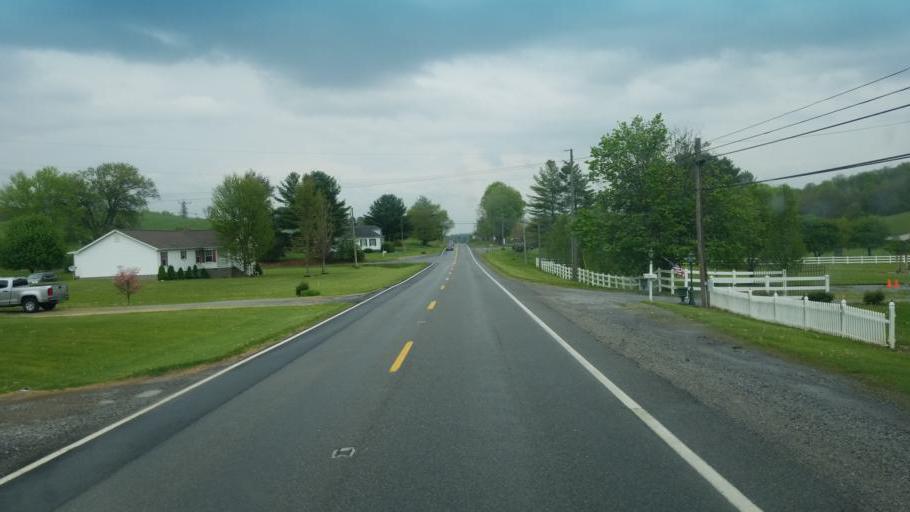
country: US
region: Virginia
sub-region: Wythe County
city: Rural Retreat
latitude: 36.9033
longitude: -81.3100
